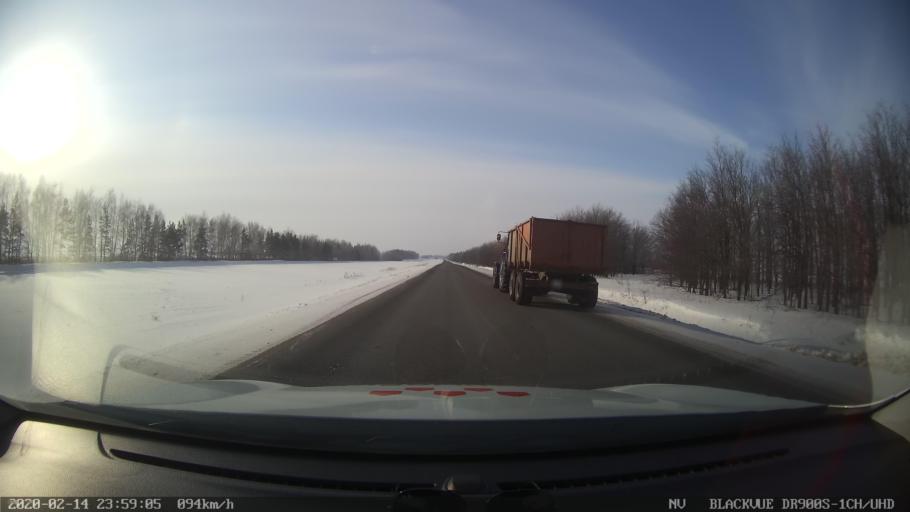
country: RU
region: Tatarstan
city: Kuybyshevskiy Zaton
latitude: 55.3422
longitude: 49.0732
